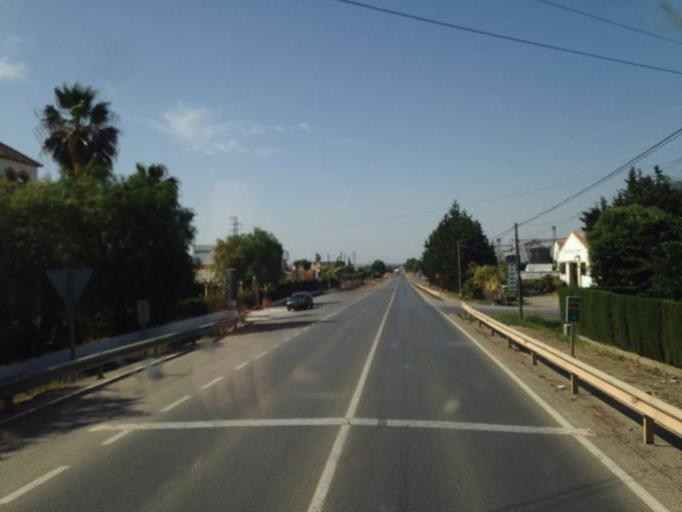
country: ES
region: Andalusia
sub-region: Provincia de Malaga
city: Antequera
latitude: 37.0292
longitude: -4.5608
